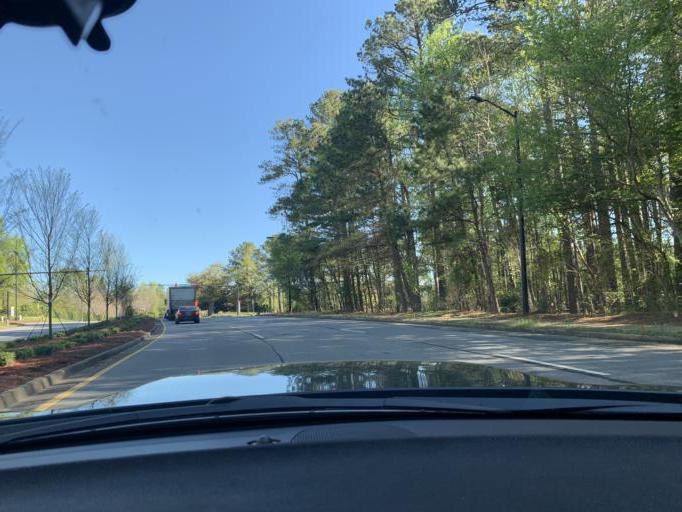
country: US
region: Georgia
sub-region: Fulton County
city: Alpharetta
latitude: 34.0887
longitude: -84.2523
